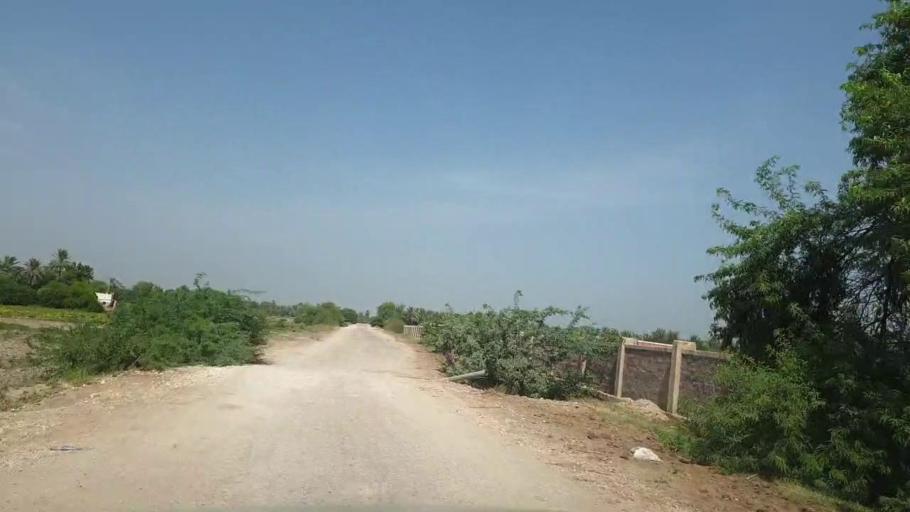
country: PK
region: Sindh
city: Rohri
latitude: 27.6888
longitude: 68.9542
